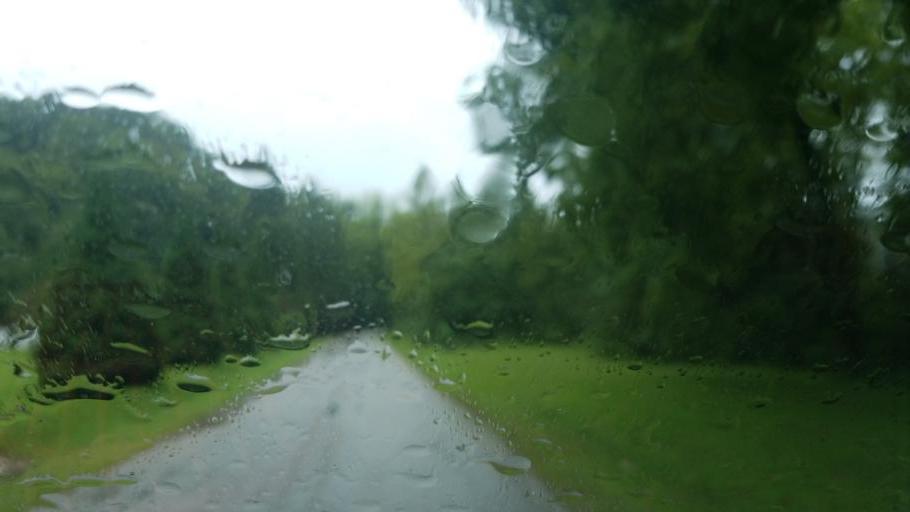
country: US
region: Ohio
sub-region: Adams County
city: Peebles
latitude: 38.8208
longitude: -83.2381
